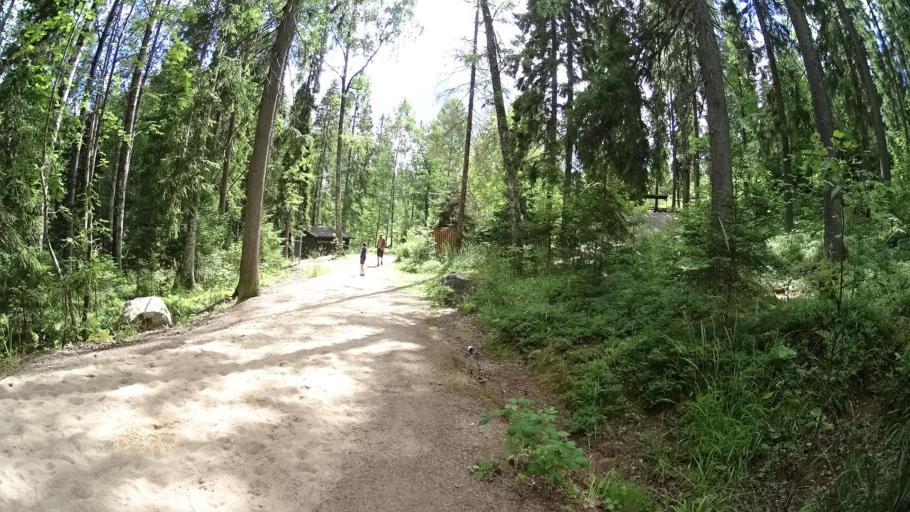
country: FI
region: Uusimaa
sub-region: Helsinki
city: Espoo
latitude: 60.2987
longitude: 24.6201
